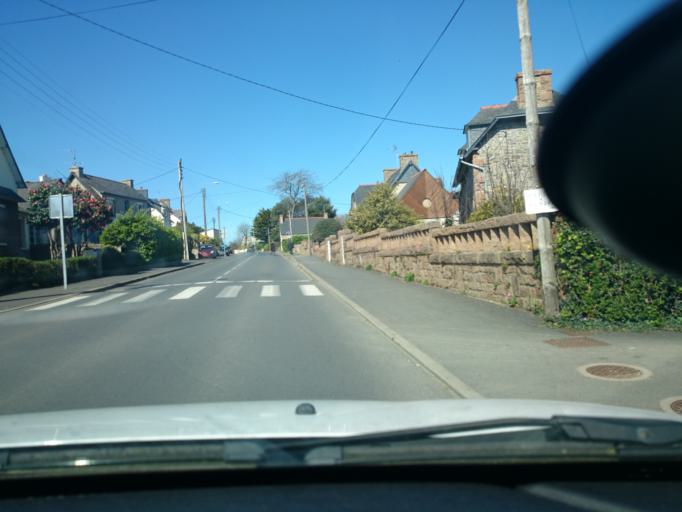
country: FR
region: Brittany
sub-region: Departement des Cotes-d'Armor
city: Tregastel
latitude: 48.8240
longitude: -3.5051
